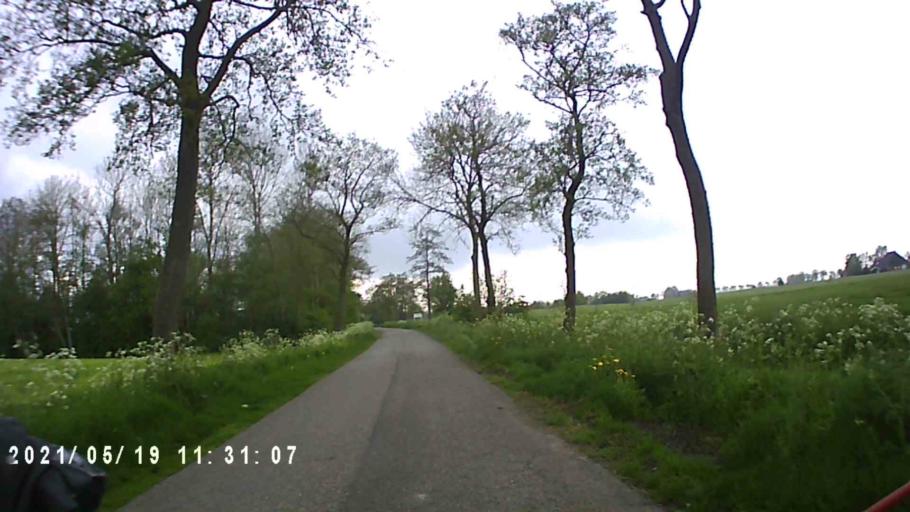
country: NL
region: Friesland
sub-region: Gemeente Kollumerland en Nieuwkruisland
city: Kollum
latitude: 53.2734
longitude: 6.1760
